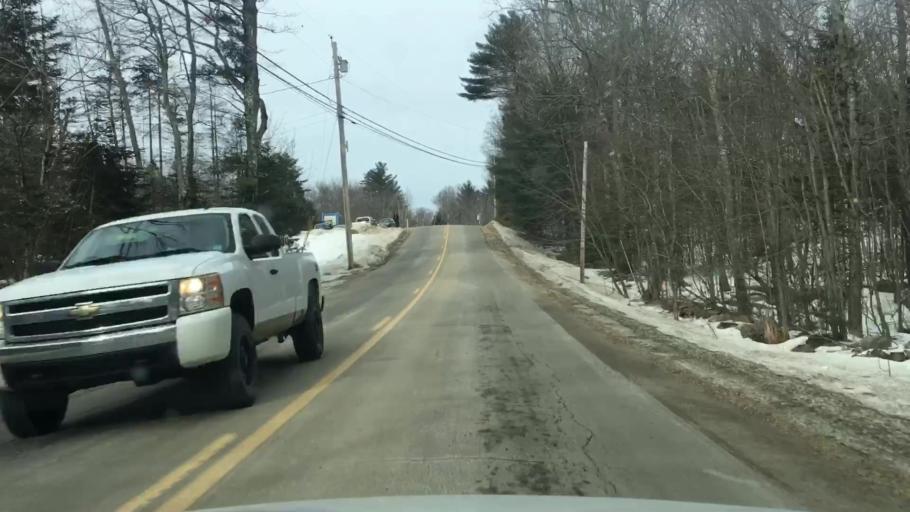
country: US
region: Maine
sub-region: Kennebec County
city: Chelsea
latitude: 44.2532
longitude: -69.6392
